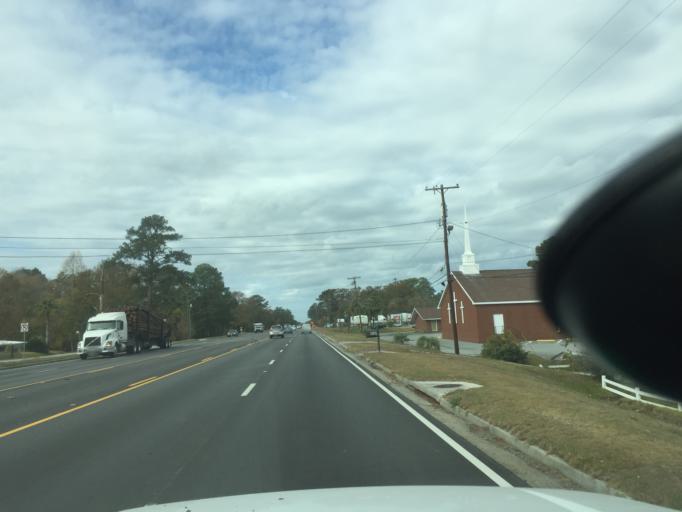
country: US
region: Georgia
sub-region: Chatham County
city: Garden City
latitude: 32.0868
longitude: -81.1699
